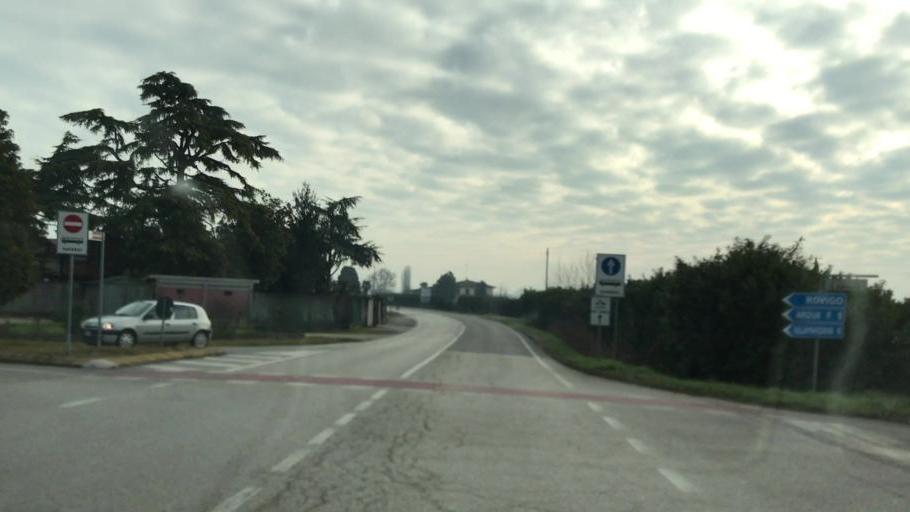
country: IT
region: Veneto
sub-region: Provincia di Rovigo
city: Fratta Polesine
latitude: 45.0270
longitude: 11.6409
